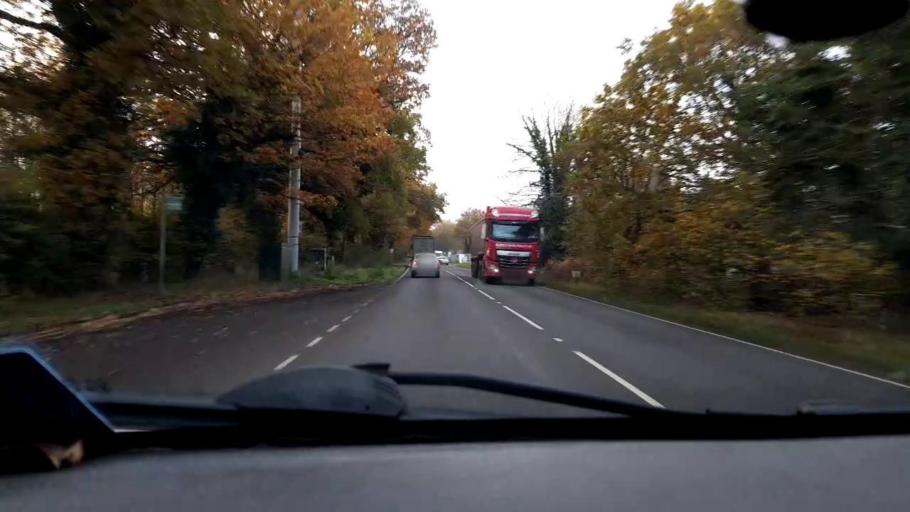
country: GB
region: England
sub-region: Norfolk
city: Costessey
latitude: 52.7171
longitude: 1.1272
